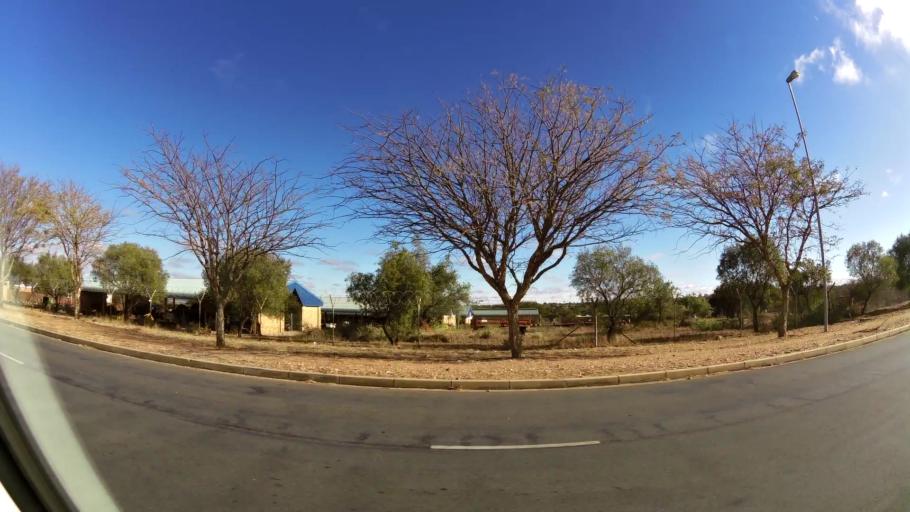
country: ZA
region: Limpopo
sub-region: Capricorn District Municipality
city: Polokwane
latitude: -23.9205
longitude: 29.4762
